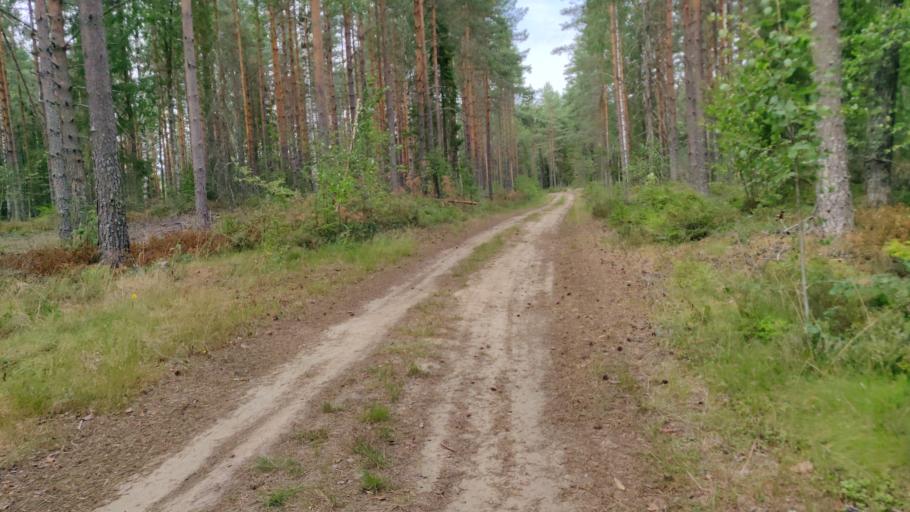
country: SE
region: Vaermland
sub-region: Hagfors Kommun
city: Hagfors
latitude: 60.0159
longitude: 13.5583
